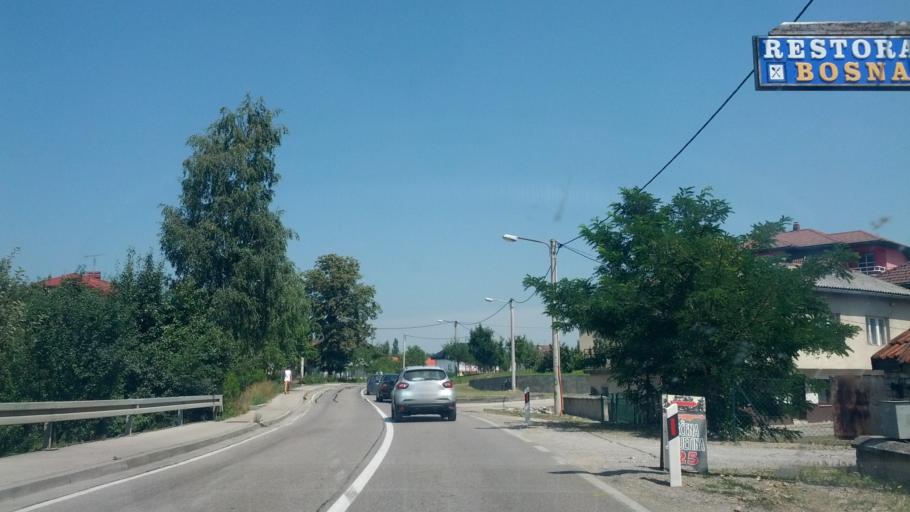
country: BA
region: Federation of Bosnia and Herzegovina
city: Bihac
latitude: 44.8408
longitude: 15.8285
